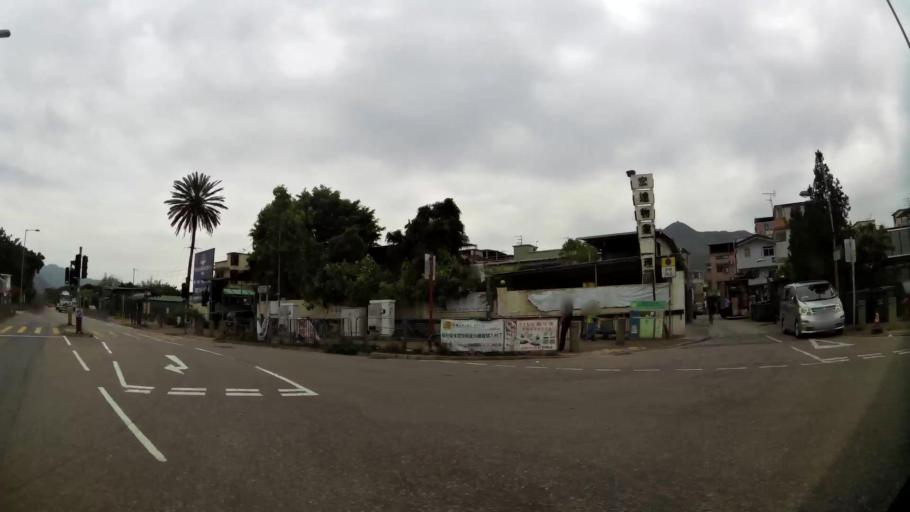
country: HK
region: Yuen Long
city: Yuen Long Kau Hui
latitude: 22.4348
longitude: 113.9927
